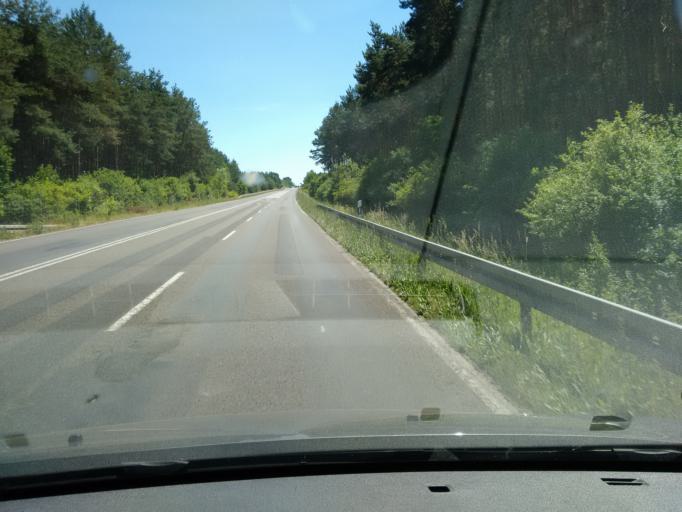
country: DE
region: Brandenburg
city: Beeskow
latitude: 52.1975
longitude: 14.2641
